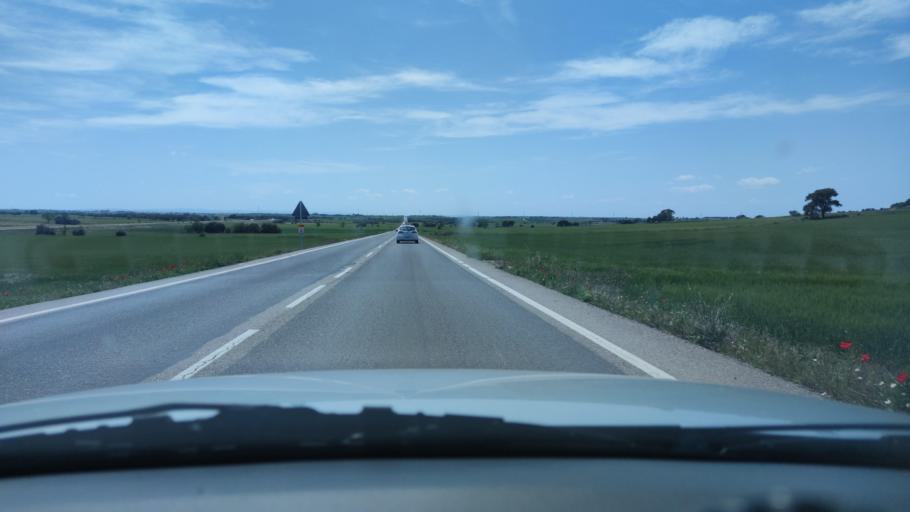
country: ES
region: Catalonia
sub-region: Provincia de Lleida
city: Mont-roig del Camp
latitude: 41.7413
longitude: 1.2219
